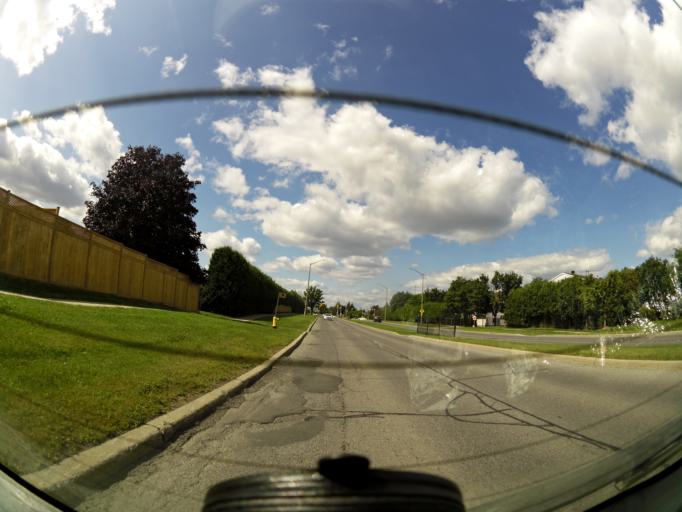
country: CA
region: Quebec
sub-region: Outaouais
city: Gatineau
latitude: 45.4589
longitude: -75.5077
